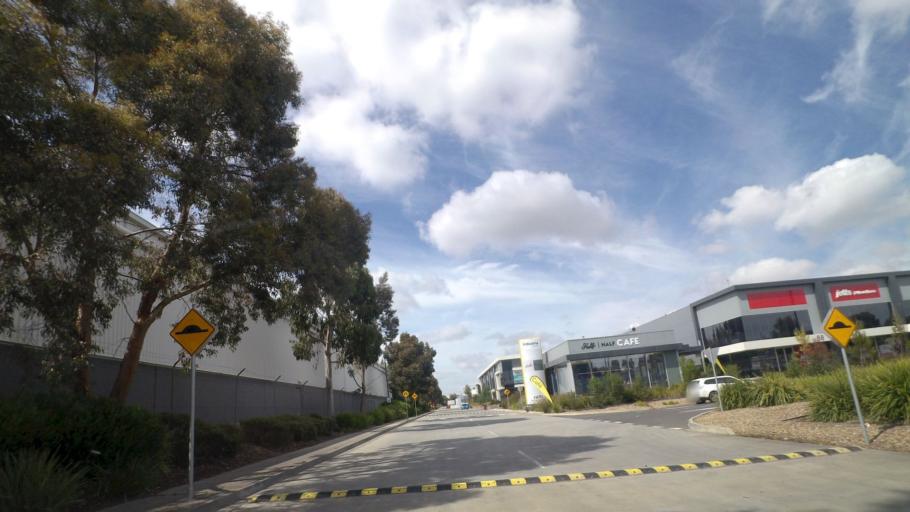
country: AU
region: Victoria
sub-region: Knox
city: Scoresby
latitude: -37.8993
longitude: 145.2431
